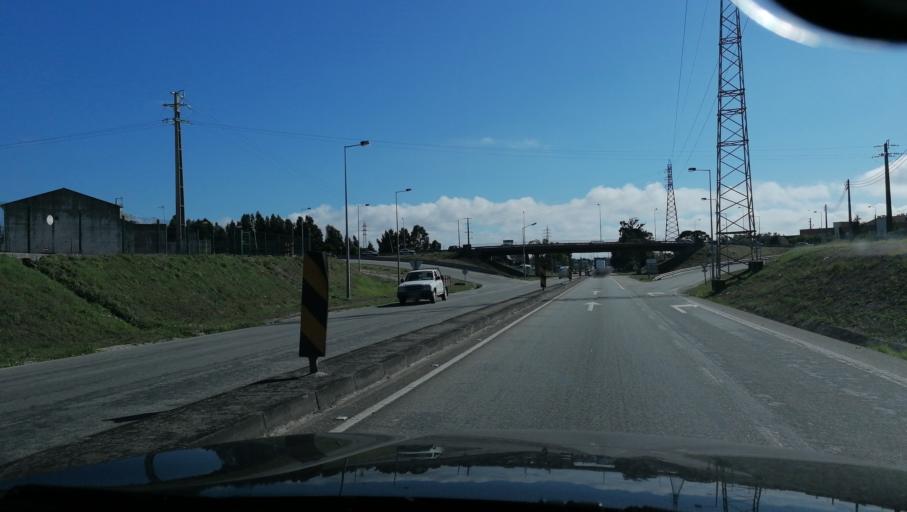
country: PT
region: Aveiro
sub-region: Aveiro
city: Aveiro
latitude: 40.6556
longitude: -8.6181
